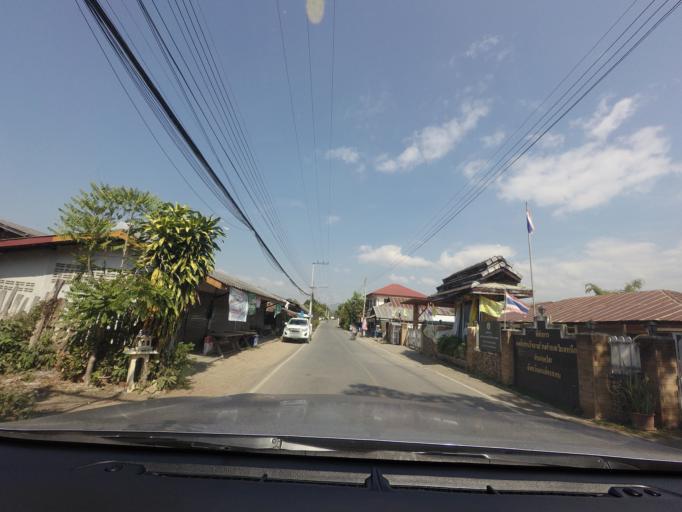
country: TH
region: Mae Hong Son
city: Wiang Nuea
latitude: 19.3784
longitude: 98.4458
